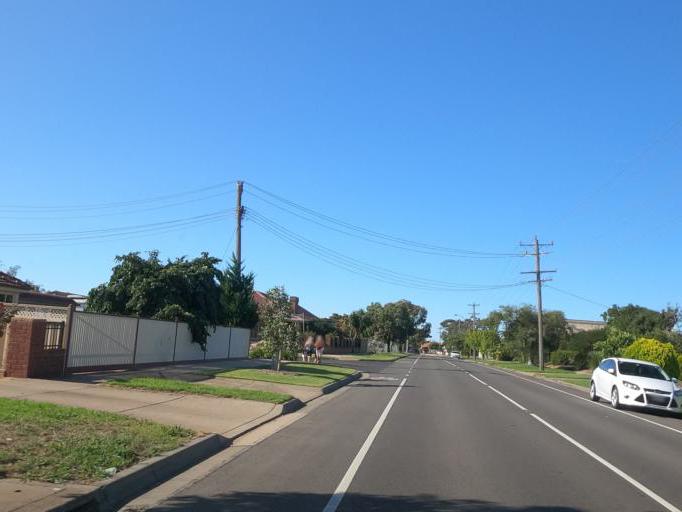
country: AU
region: Victoria
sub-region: Hume
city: Attwood
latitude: -37.6476
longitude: 144.8898
